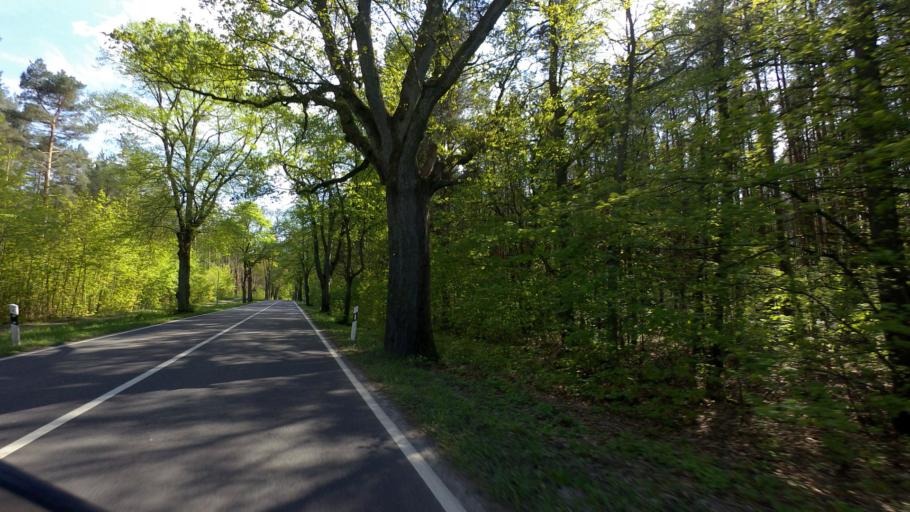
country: DE
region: Brandenburg
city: Milmersdorf
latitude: 53.0460
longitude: 13.6034
